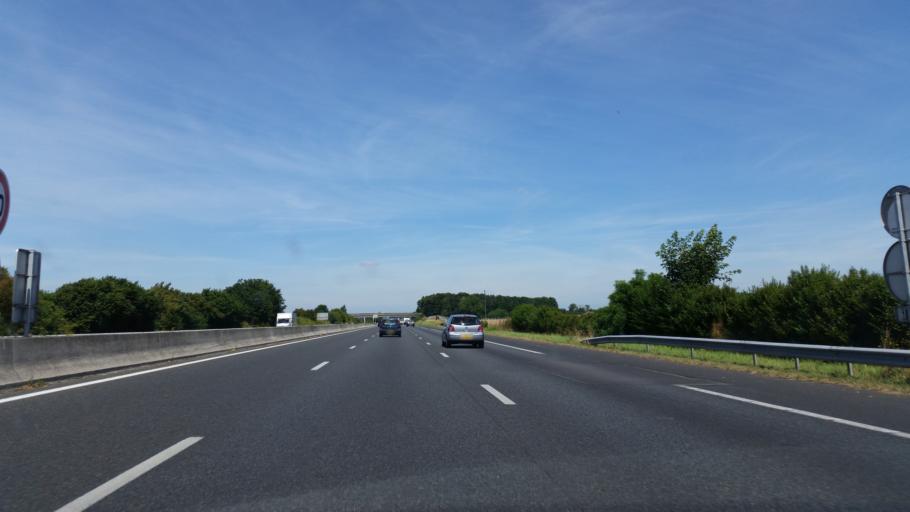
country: FR
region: Nord-Pas-de-Calais
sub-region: Departement du Pas-de-Calais
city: Bapaume
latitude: 50.1203
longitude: 2.8718
